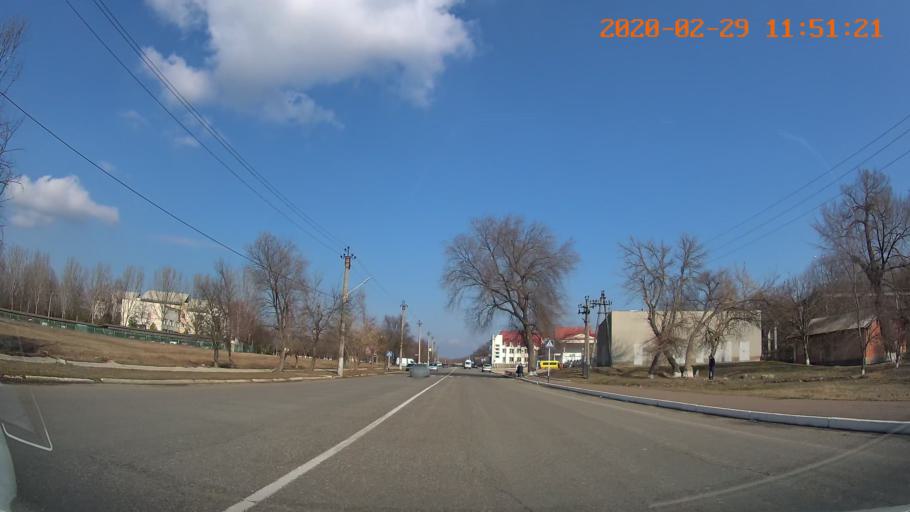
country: MD
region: Telenesti
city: Ribnita
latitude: 47.7647
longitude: 28.9900
